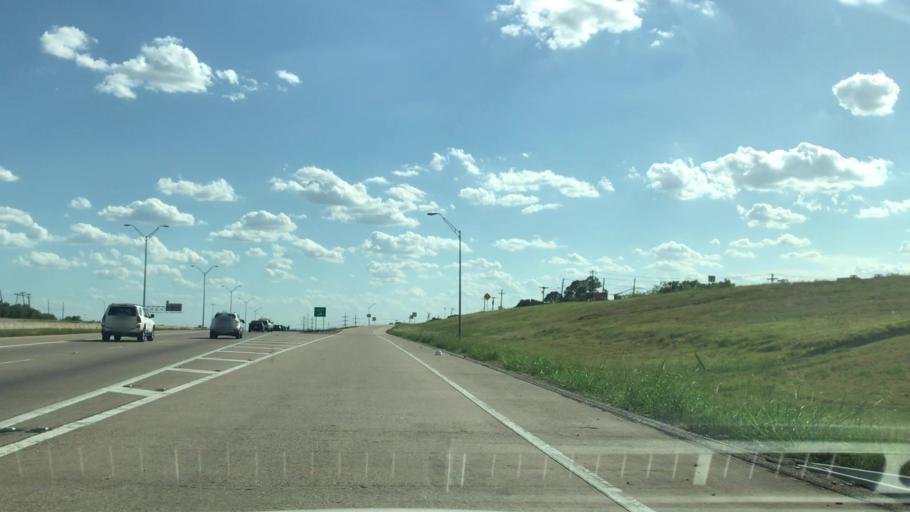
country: US
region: Texas
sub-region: Dallas County
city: Irving
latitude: 32.8636
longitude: -97.0058
